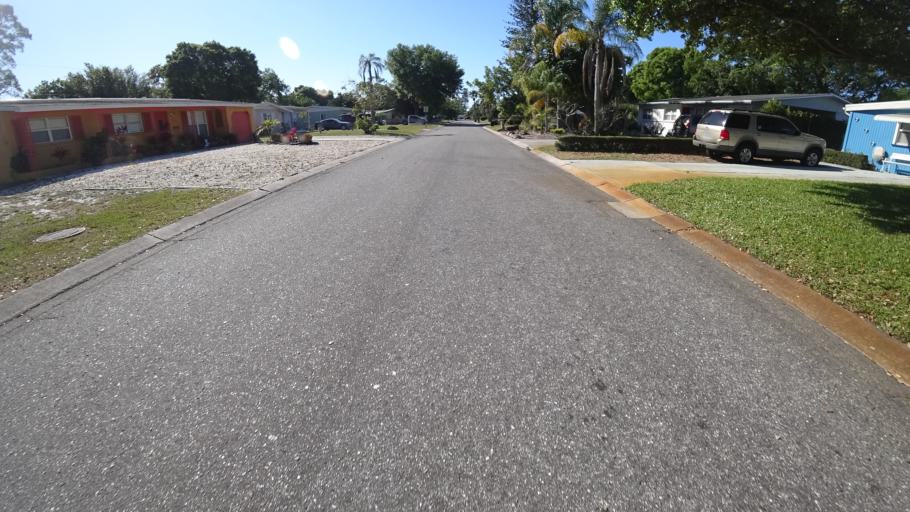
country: US
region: Florida
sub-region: Manatee County
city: Bayshore Gardens
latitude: 27.4258
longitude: -82.5902
